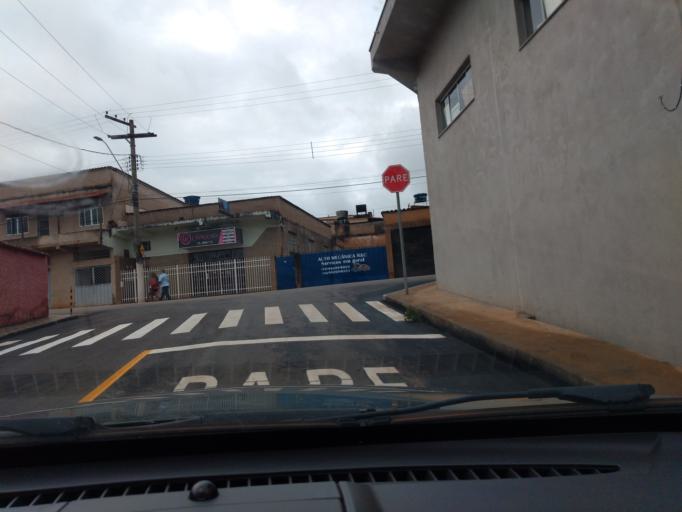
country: BR
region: Minas Gerais
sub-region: Lavras
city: Lavras
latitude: -21.5108
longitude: -44.9051
